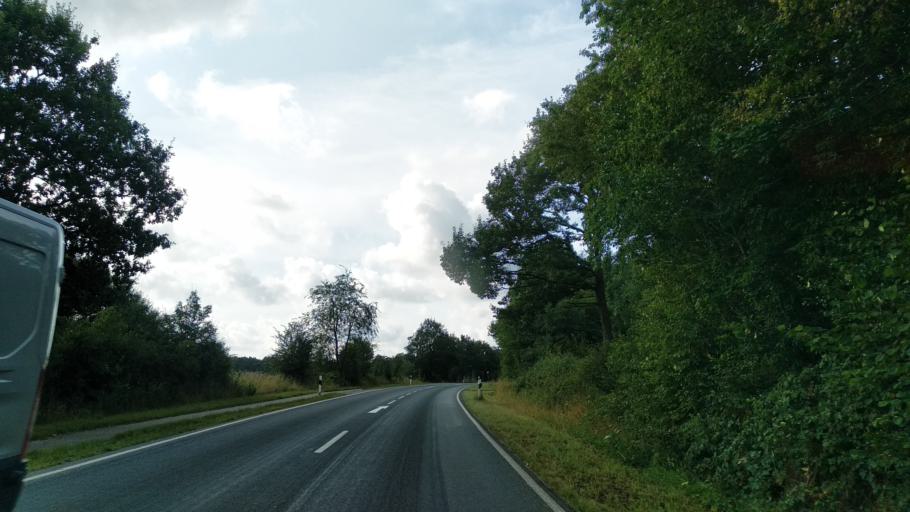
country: DE
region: Schleswig-Holstein
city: Selk
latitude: 54.4792
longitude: 9.5663
